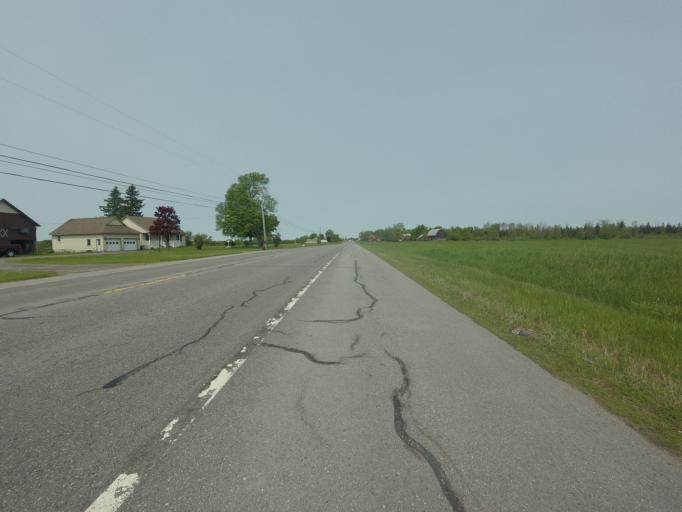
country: US
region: New York
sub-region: Jefferson County
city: Dexter
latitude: 44.0458
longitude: -76.0890
